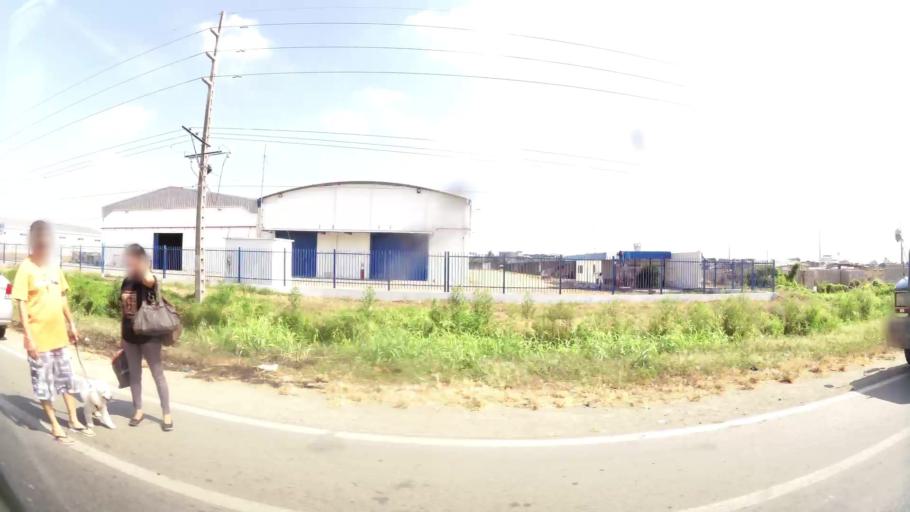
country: EC
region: Guayas
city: Eloy Alfaro
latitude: -2.1783
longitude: -79.8036
